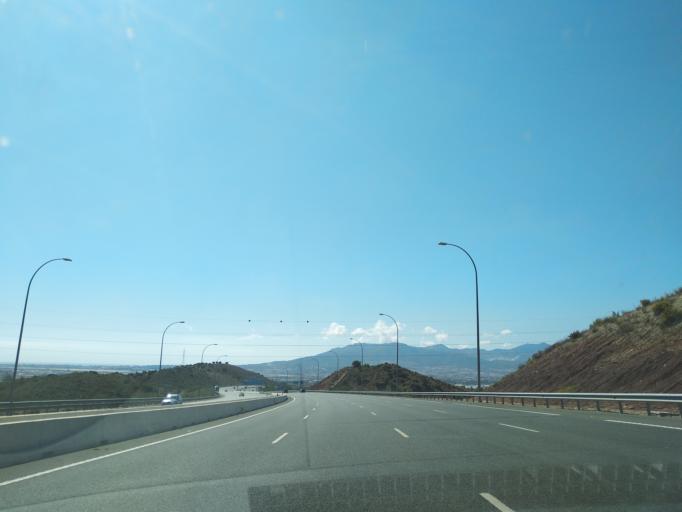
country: ES
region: Andalusia
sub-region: Provincia de Malaga
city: Malaga
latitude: 36.7342
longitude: -4.5068
